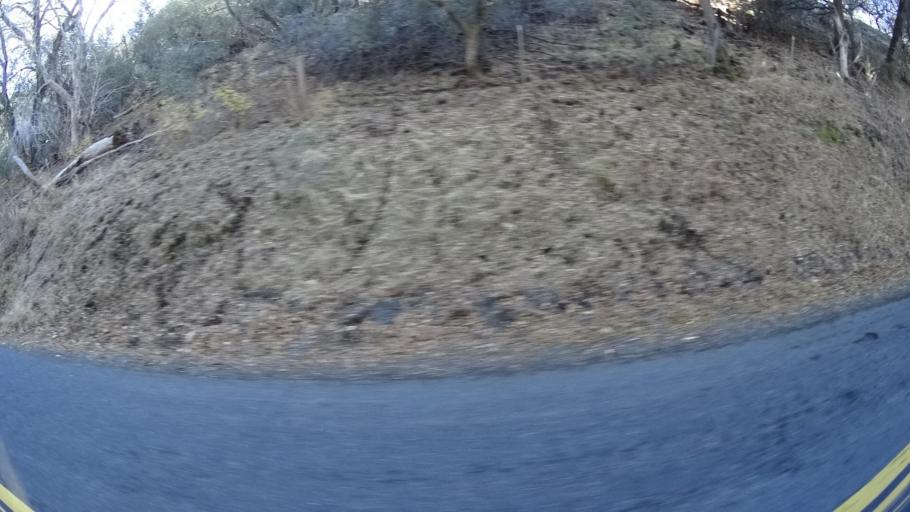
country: US
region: California
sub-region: Kern County
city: Alta Sierra
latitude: 35.7894
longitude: -118.7456
